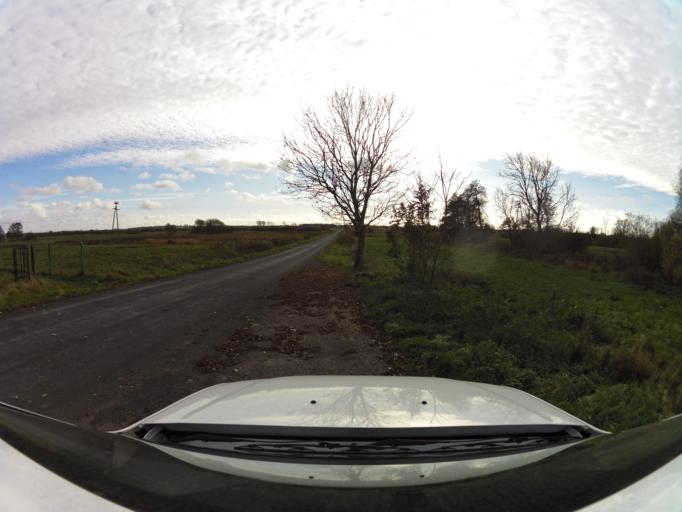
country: PL
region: West Pomeranian Voivodeship
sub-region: Powiat gryficki
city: Trzebiatow
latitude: 54.0784
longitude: 15.1729
